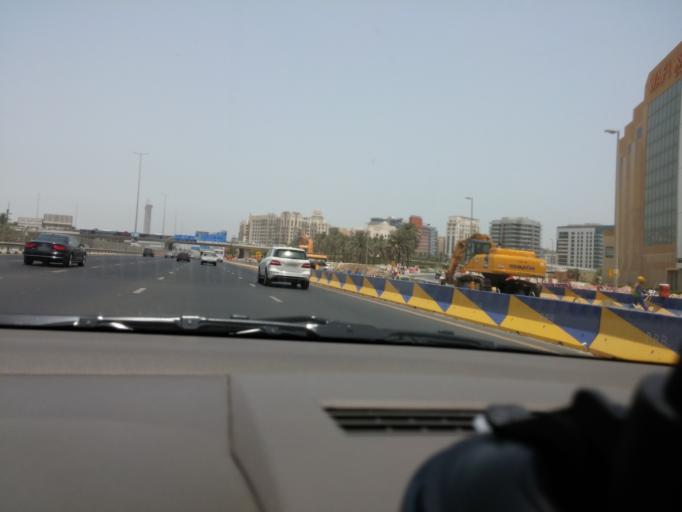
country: AE
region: Ash Shariqah
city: Sharjah
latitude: 25.2280
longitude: 55.3183
